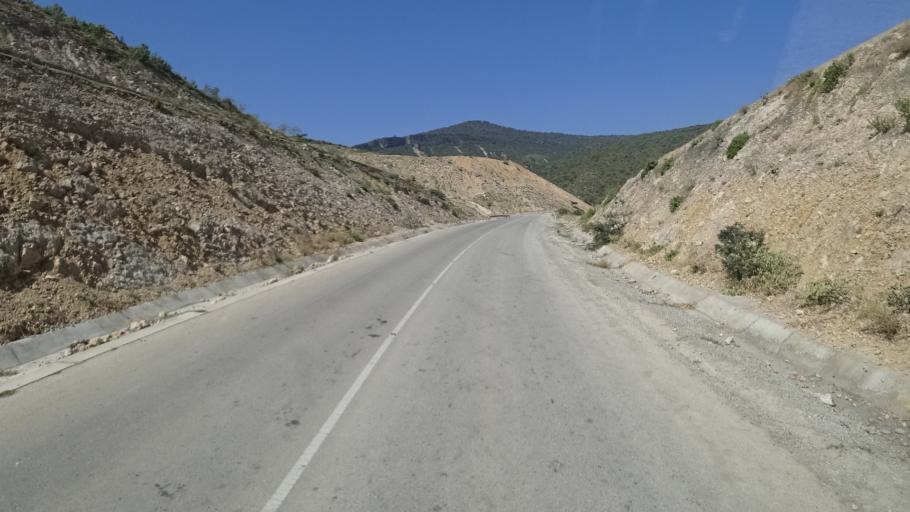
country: OM
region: Zufar
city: Salalah
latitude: 17.0452
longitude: 54.6129
